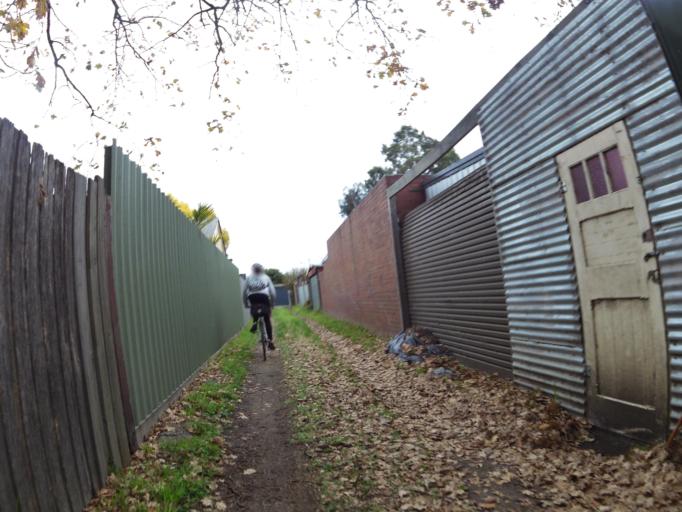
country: AU
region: Victoria
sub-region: Moreland
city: Pascoe Vale South
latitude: -37.7424
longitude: 144.9525
